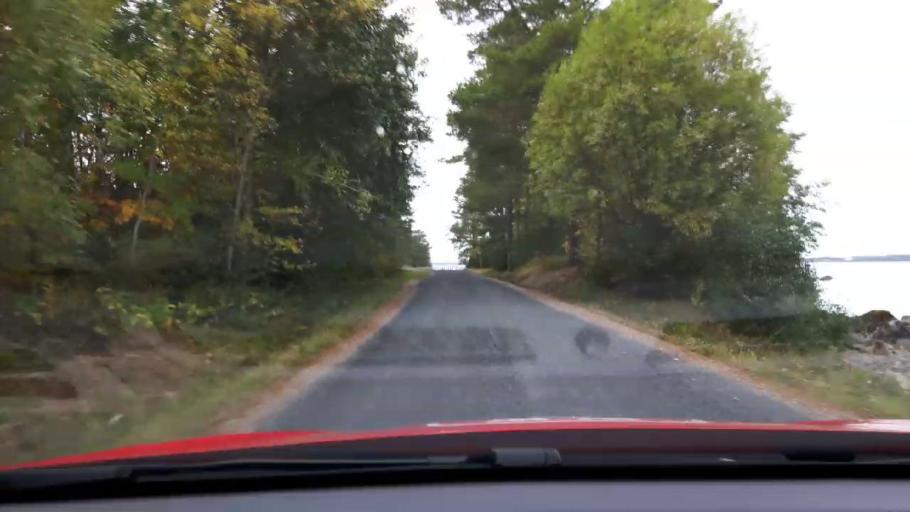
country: SE
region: Jaemtland
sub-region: Krokoms Kommun
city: Krokom
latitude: 63.1594
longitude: 14.1667
